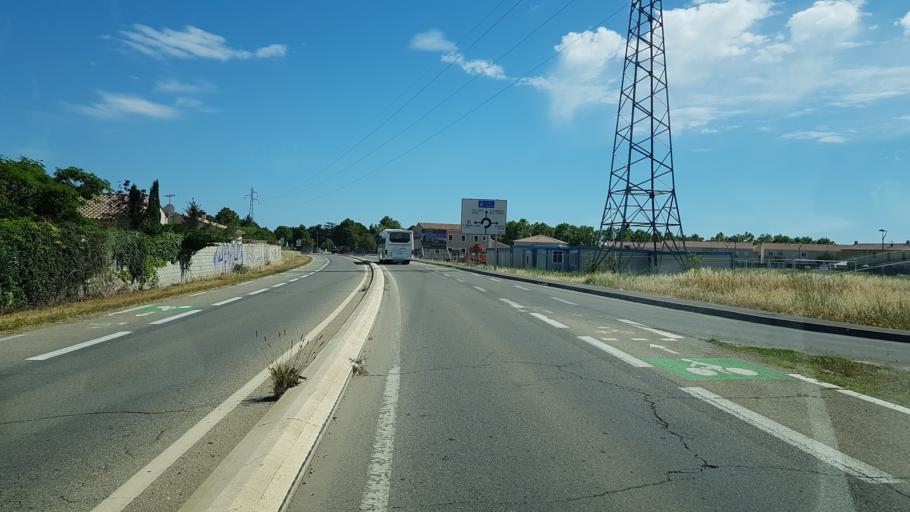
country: FR
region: Provence-Alpes-Cote d'Azur
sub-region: Departement des Bouches-du-Rhone
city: Saint-Martin-de-Crau
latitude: 43.6396
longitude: 4.7983
